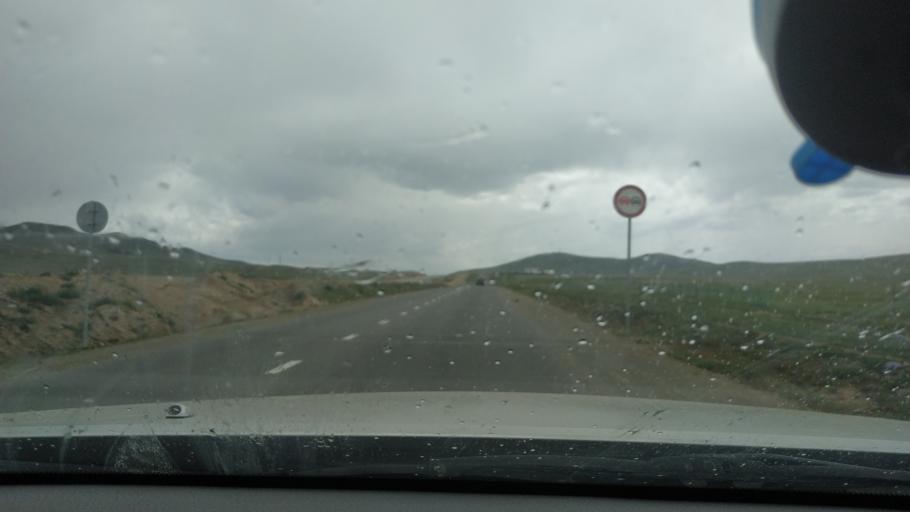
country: MN
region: Ulaanbaatar
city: Ulaanbaatar
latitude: 47.8103
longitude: 106.7523
